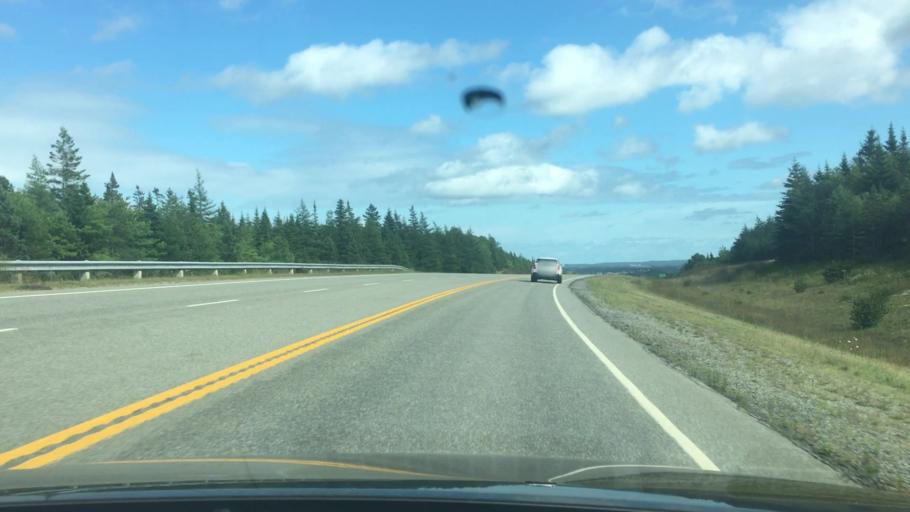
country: CA
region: Nova Scotia
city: Port Hawkesbury
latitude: 45.6219
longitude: -61.1206
